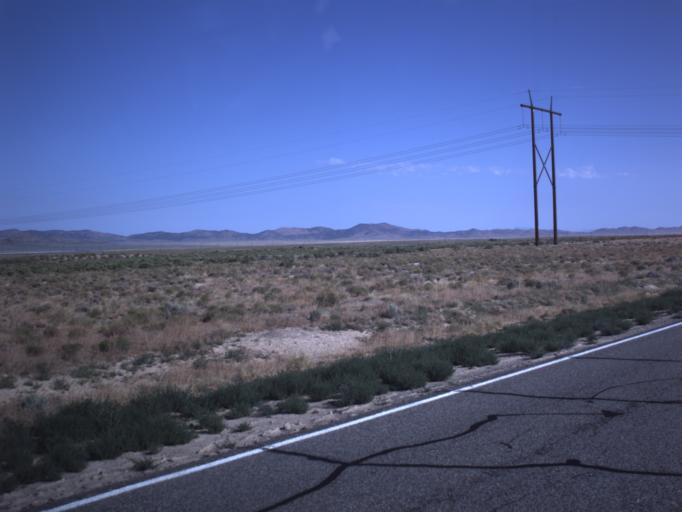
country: US
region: Utah
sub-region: Beaver County
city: Milford
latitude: 38.4868
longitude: -112.9911
